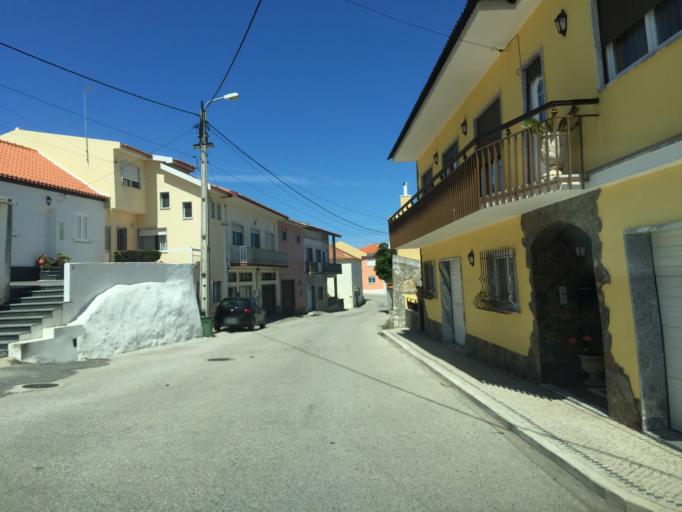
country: PT
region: Lisbon
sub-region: Lourinha
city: Lourinha
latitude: 39.2034
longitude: -9.3323
